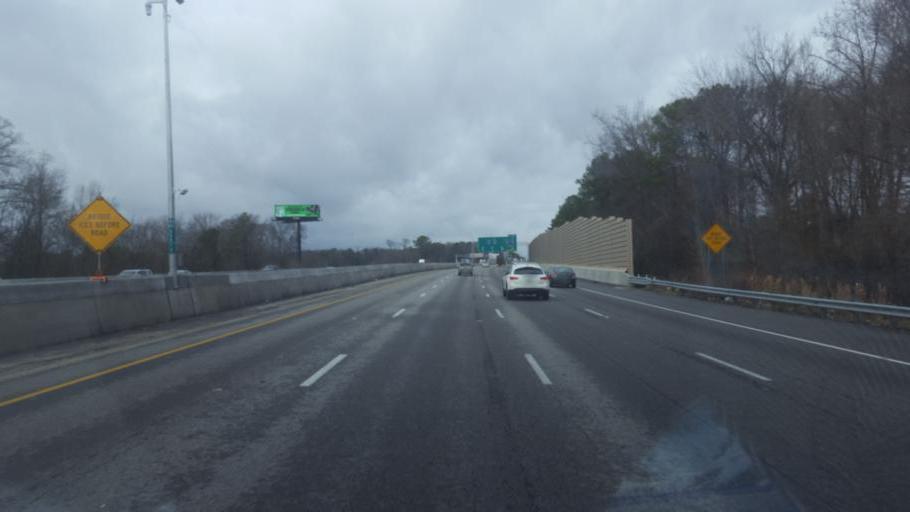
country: US
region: Georgia
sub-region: Henry County
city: Stockbridge
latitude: 33.5151
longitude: -84.2421
